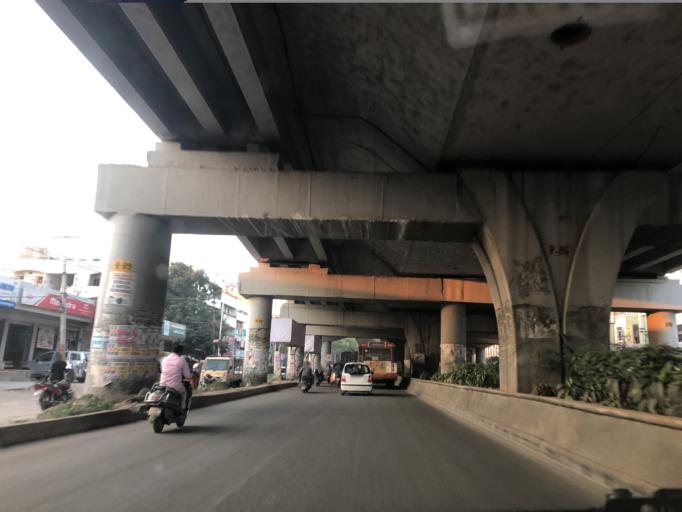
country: IN
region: Telangana
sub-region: Hyderabad
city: Hyderabad
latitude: 17.3817
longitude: 78.4293
